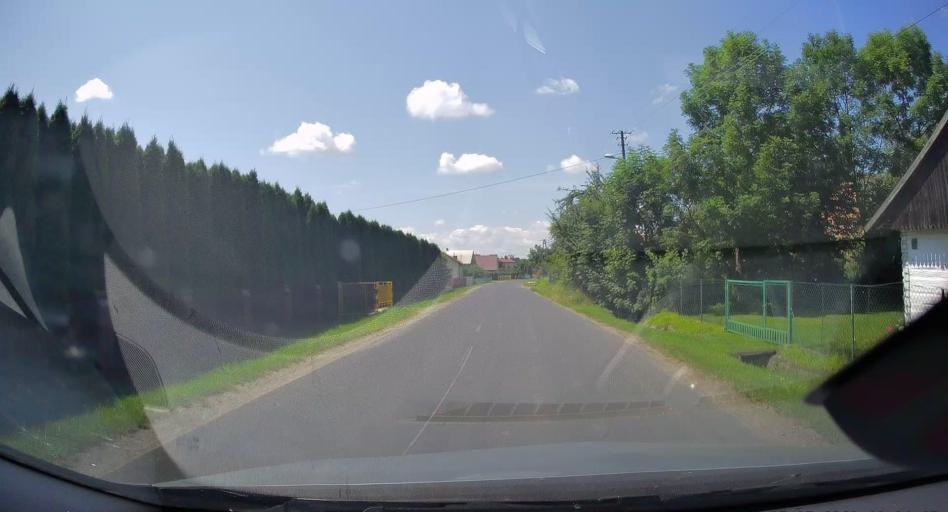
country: PL
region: Subcarpathian Voivodeship
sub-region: Powiat przemyski
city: Medyka
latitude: 49.8357
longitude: 22.8806
